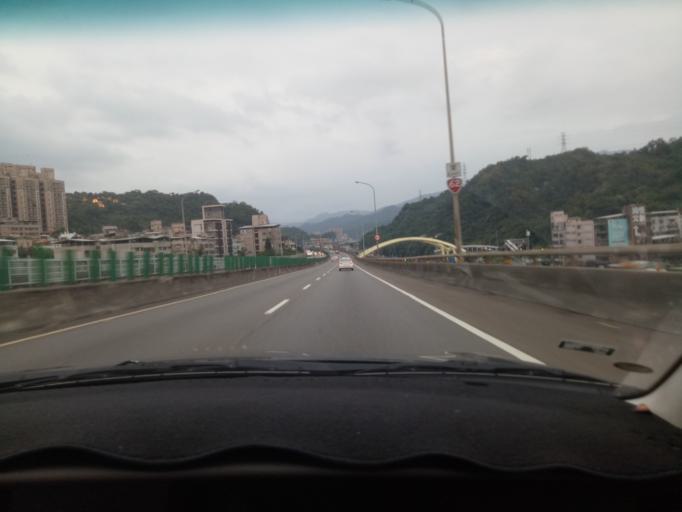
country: TW
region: Taiwan
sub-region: Keelung
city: Keelung
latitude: 25.1041
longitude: 121.7376
